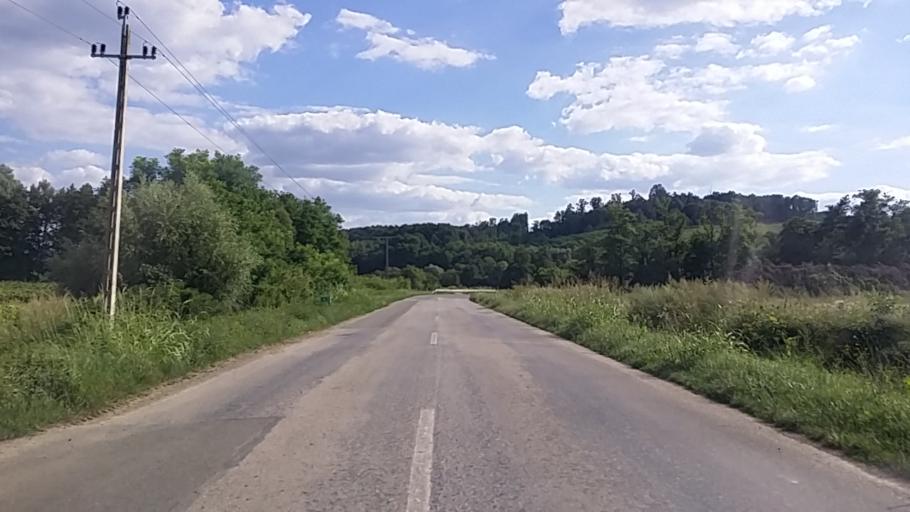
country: HU
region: Baranya
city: Sasd
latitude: 46.1884
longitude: 18.0823
